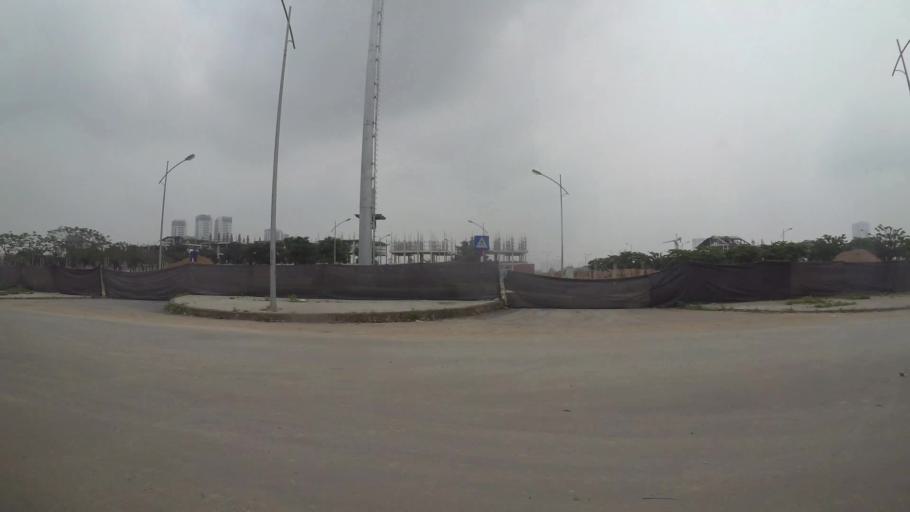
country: VN
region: Ha Noi
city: Ha Dong
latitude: 20.9834
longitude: 105.7540
